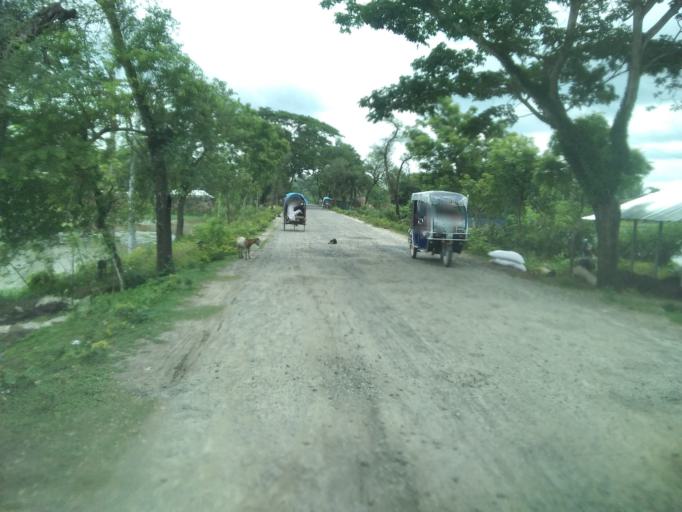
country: IN
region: West Bengal
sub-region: North 24 Parganas
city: Gosaba
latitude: 22.2683
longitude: 89.1630
